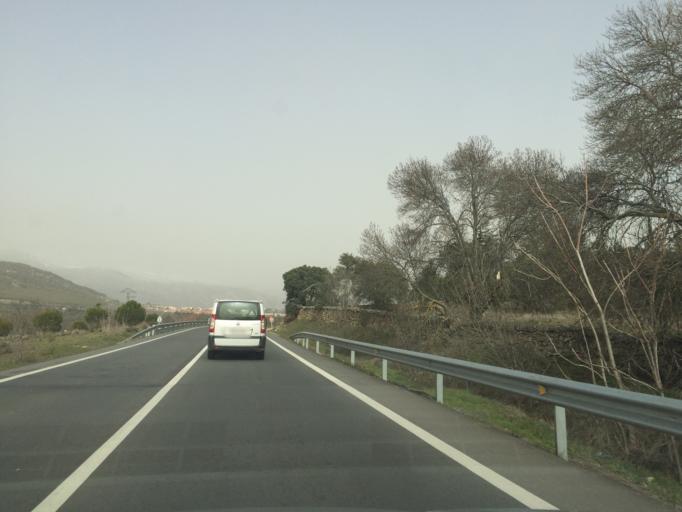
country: ES
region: Madrid
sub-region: Provincia de Madrid
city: Collado-Villalba
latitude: 40.6529
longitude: -3.9875
